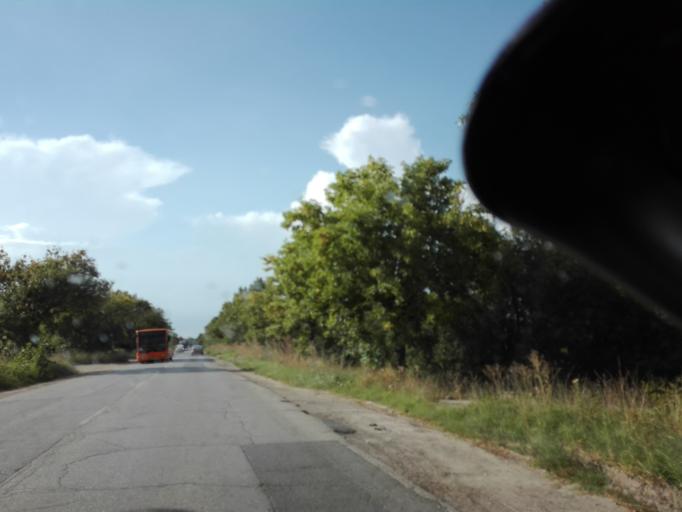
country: BG
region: Sofia-Capital
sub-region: Stolichna Obshtina
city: Sofia
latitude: 42.6241
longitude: 23.4486
